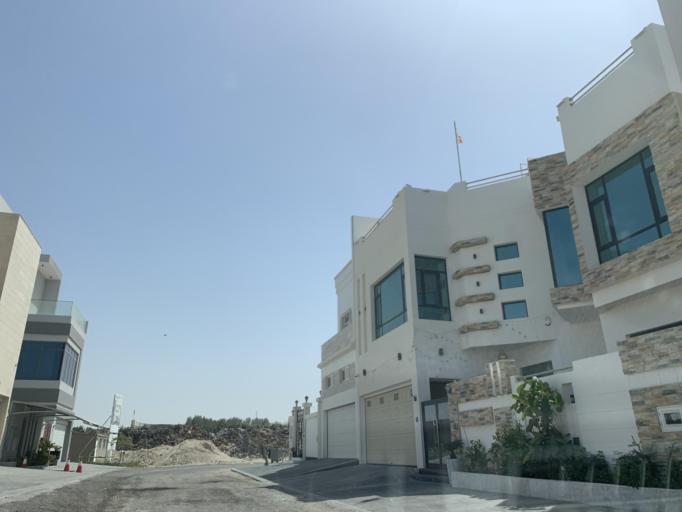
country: BH
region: Northern
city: Madinat `Isa
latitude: 26.1520
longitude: 50.5497
